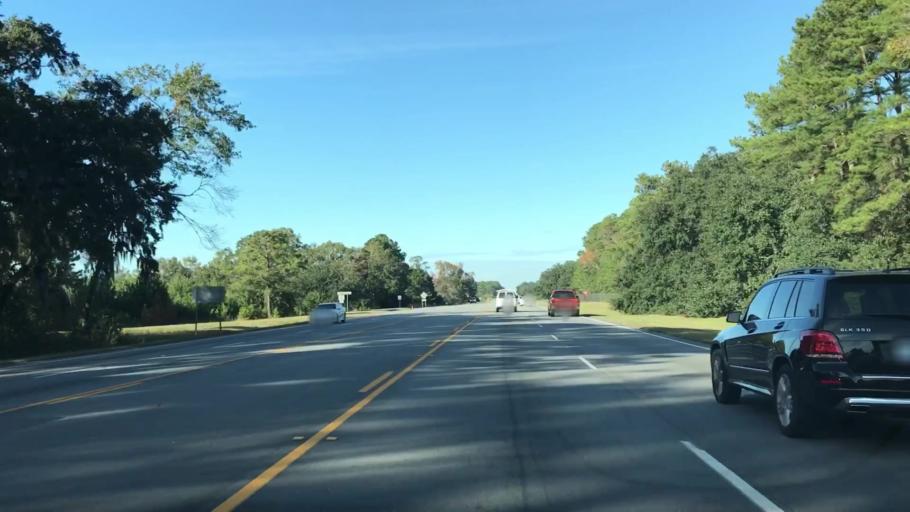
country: US
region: South Carolina
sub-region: Beaufort County
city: Burton
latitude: 32.4589
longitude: -80.7339
